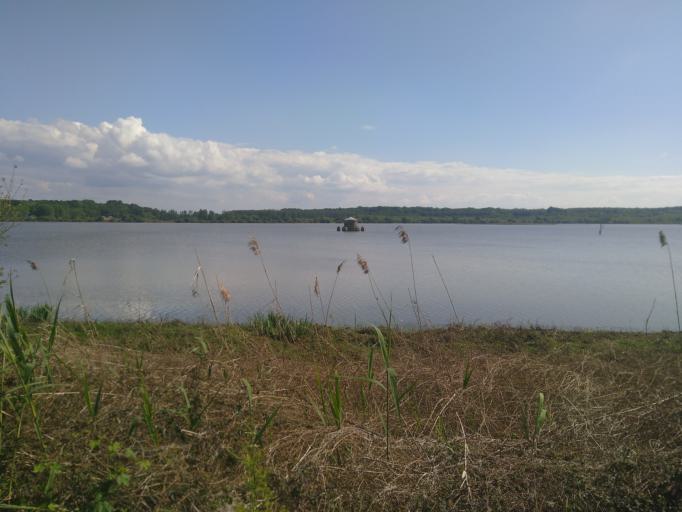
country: FR
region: Aquitaine
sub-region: Departement des Landes
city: Labenne
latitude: 43.5892
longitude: -1.3989
